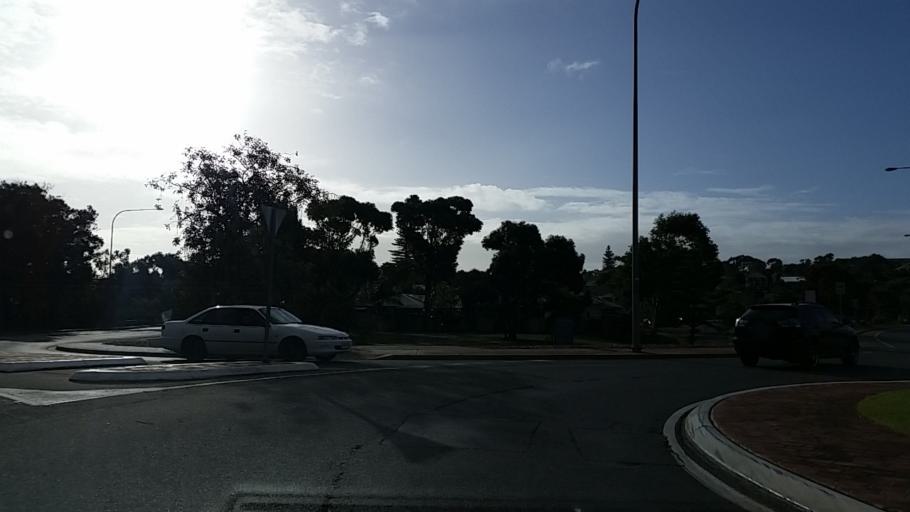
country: AU
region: South Australia
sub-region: Adelaide
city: Port Noarlunga
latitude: -35.1510
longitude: 138.4723
